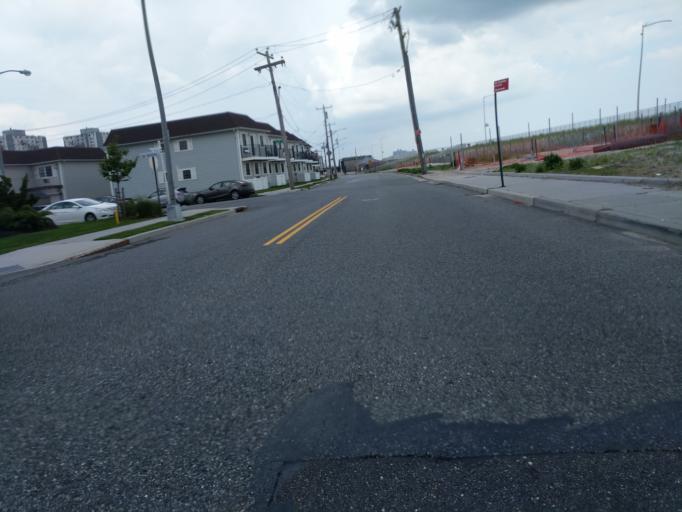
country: US
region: New York
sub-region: Nassau County
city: Inwood
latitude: 40.5885
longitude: -73.7913
